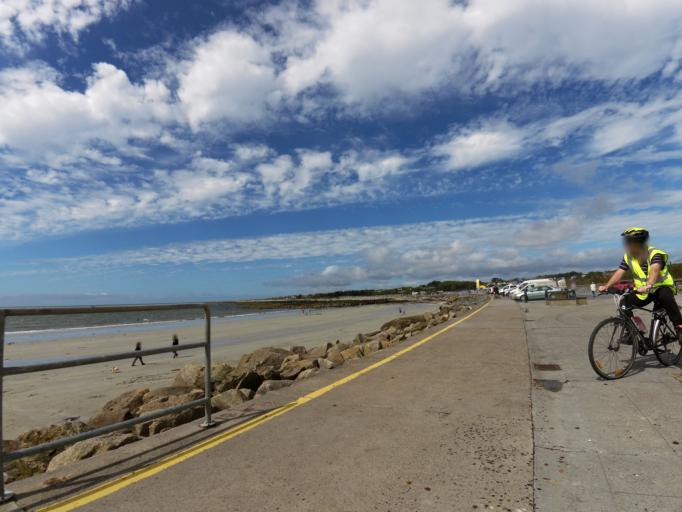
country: IE
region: Connaught
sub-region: County Galway
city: Bearna
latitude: 53.2508
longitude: -9.1245
